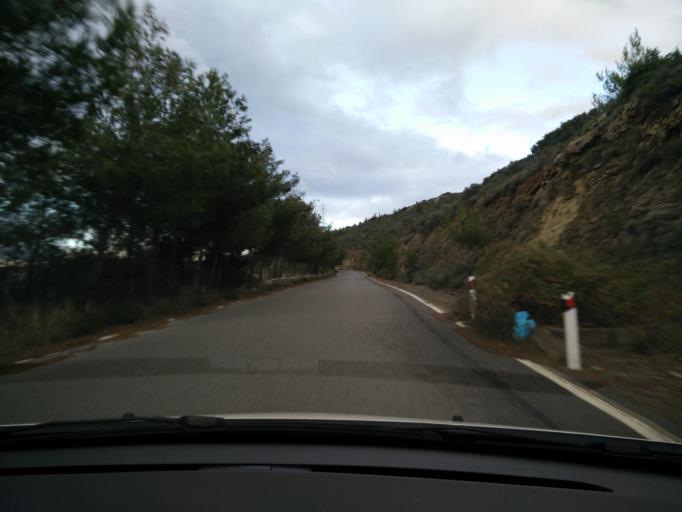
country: GR
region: Crete
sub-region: Nomos Lasithiou
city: Gra Liyia
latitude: 35.0895
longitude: 25.6982
